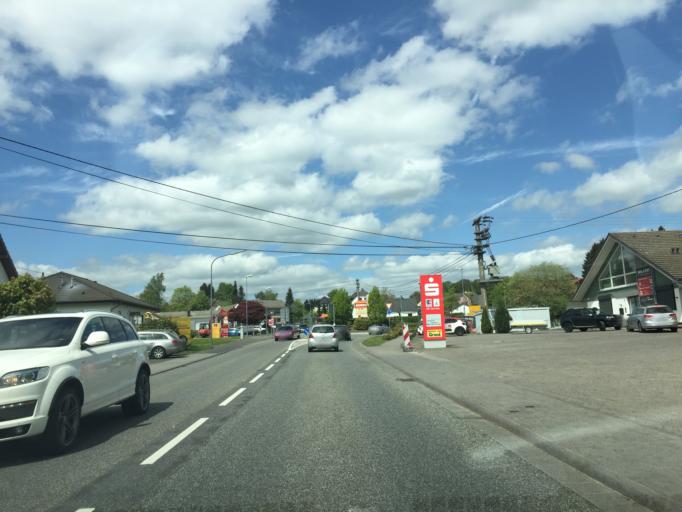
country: DE
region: Rheinland-Pfalz
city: Langenhahn
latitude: 50.5845
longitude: 7.9178
